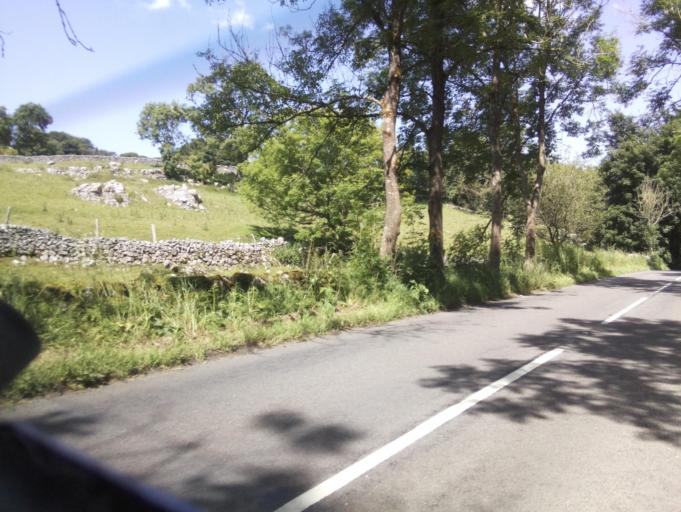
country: GB
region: England
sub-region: Derbyshire
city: Tideswell
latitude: 53.2457
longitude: -1.8085
